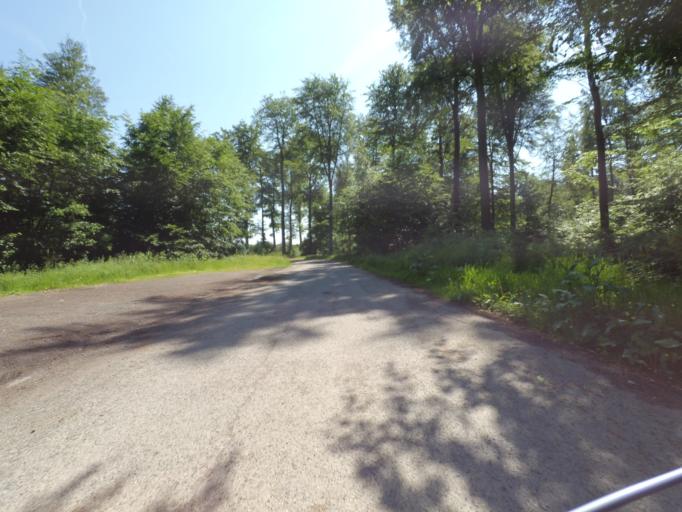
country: DE
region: Rheinland-Pfalz
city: Hollnich
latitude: 50.0643
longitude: 7.4751
